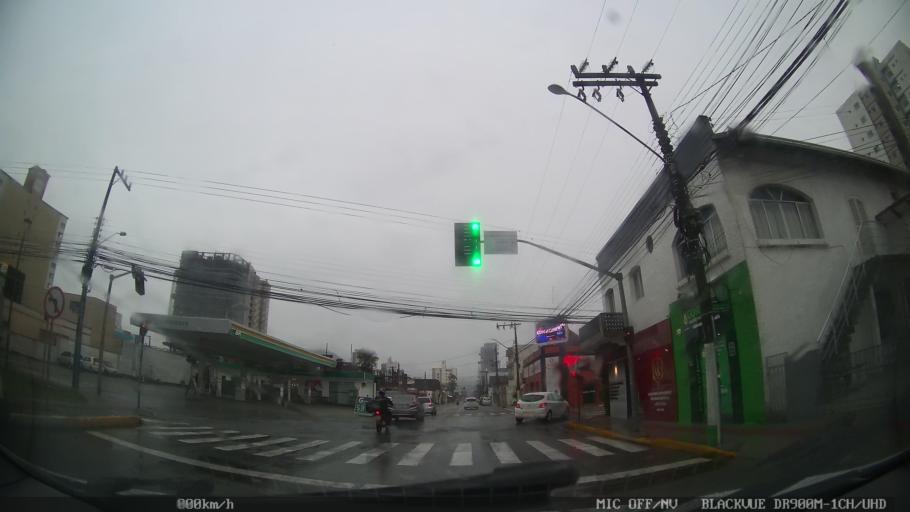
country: BR
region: Santa Catarina
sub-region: Itajai
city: Itajai
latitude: -26.9058
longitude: -48.6698
